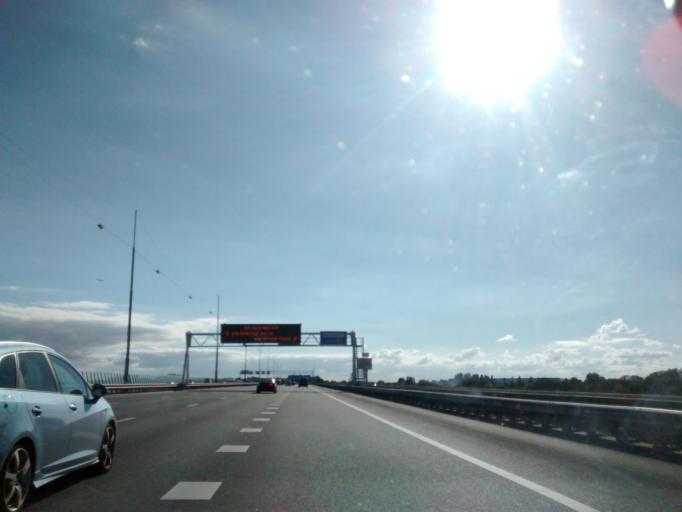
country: NL
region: North Holland
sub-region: Gemeente Diemen
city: Diemen
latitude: 52.3598
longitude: 4.9679
